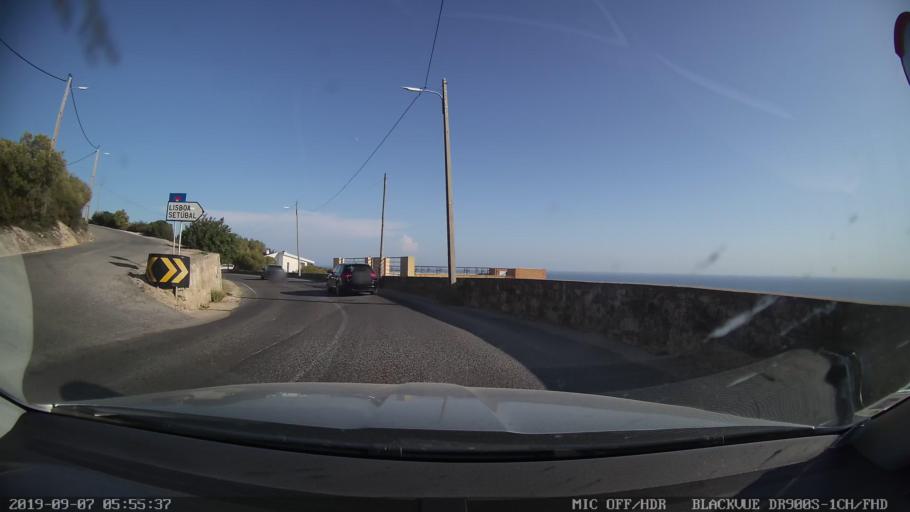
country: PT
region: Setubal
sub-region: Sesimbra
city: Sesimbra
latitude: 38.4406
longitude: -9.0887
